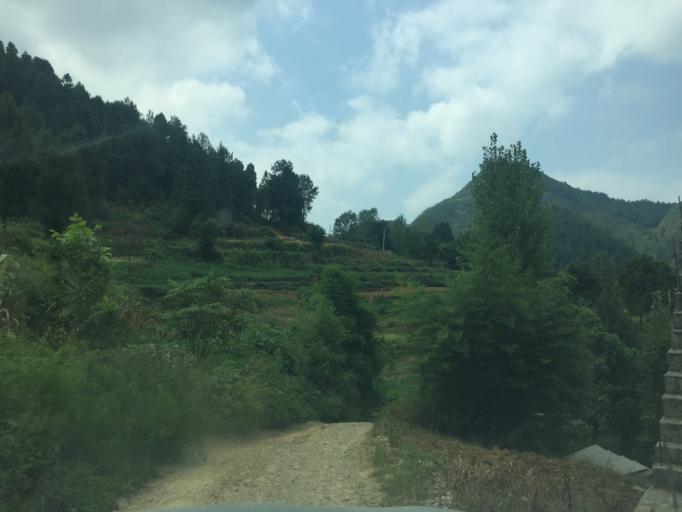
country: CN
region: Guizhou Sheng
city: Dabachang
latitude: 27.7957
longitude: 108.4058
